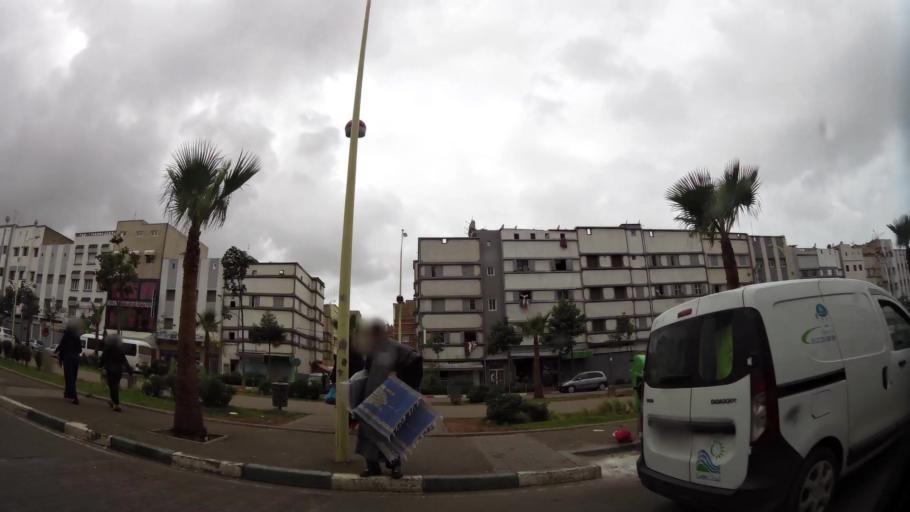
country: MA
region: Grand Casablanca
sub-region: Mediouna
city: Tit Mellil
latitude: 33.6067
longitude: -7.5103
